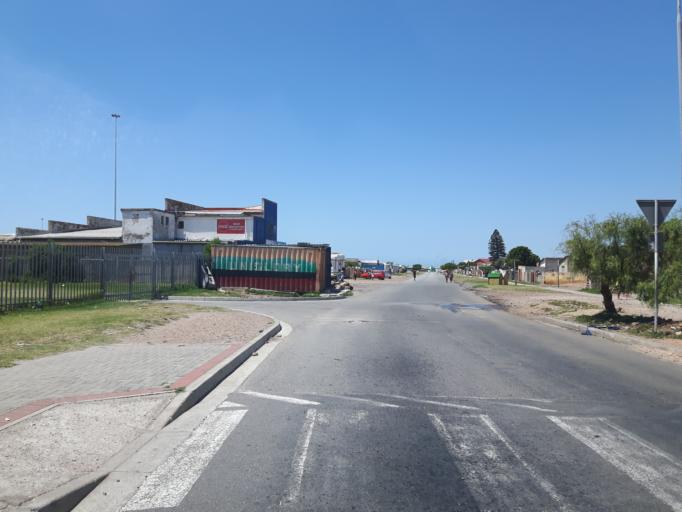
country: ZA
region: Eastern Cape
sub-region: Nelson Mandela Bay Metropolitan Municipality
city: Port Elizabeth
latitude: -33.8925
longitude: 25.6023
